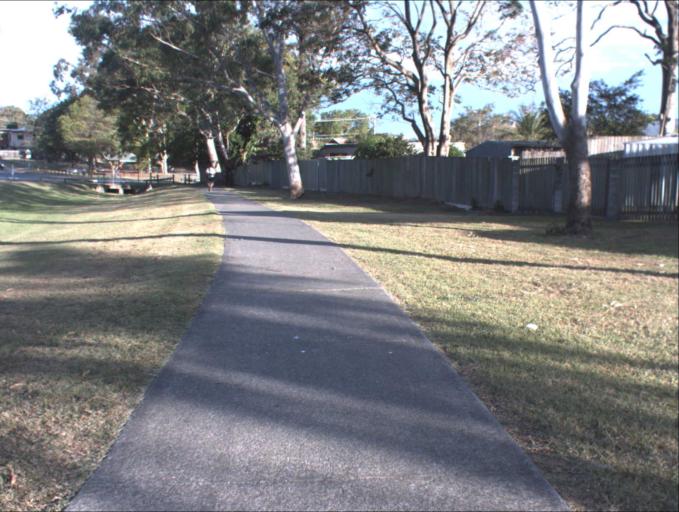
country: AU
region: Queensland
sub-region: Logan
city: Springwood
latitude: -27.6309
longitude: 153.1382
